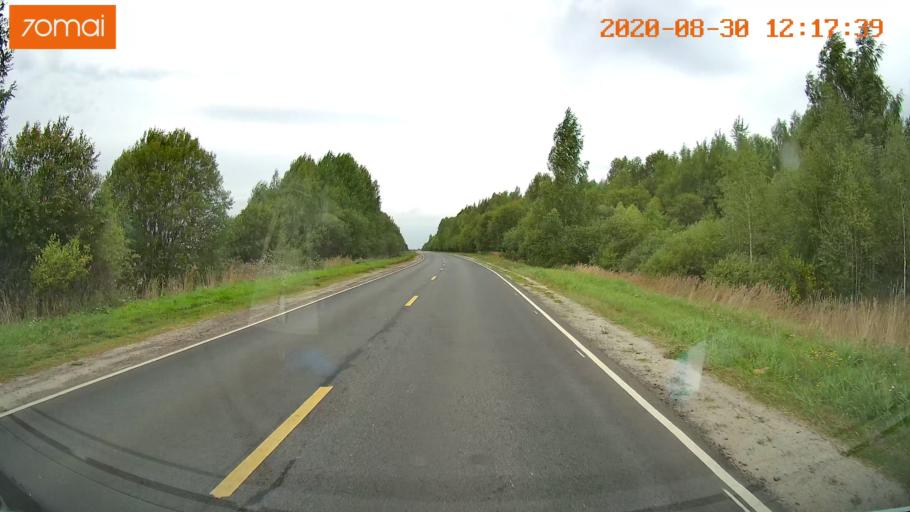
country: RU
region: Ivanovo
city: Yur'yevets
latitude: 57.3237
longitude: 42.9724
